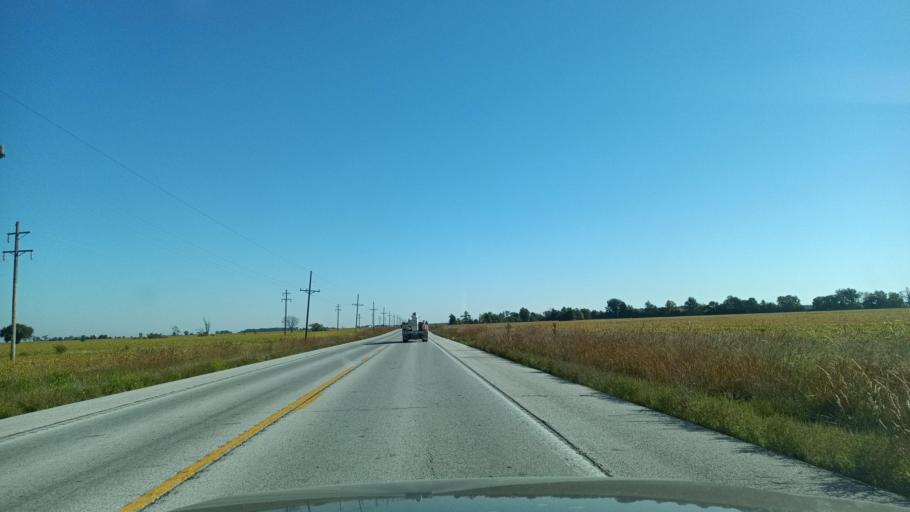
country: US
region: Missouri
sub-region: Audrain County
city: Vandalia
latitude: 39.4667
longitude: -91.6024
